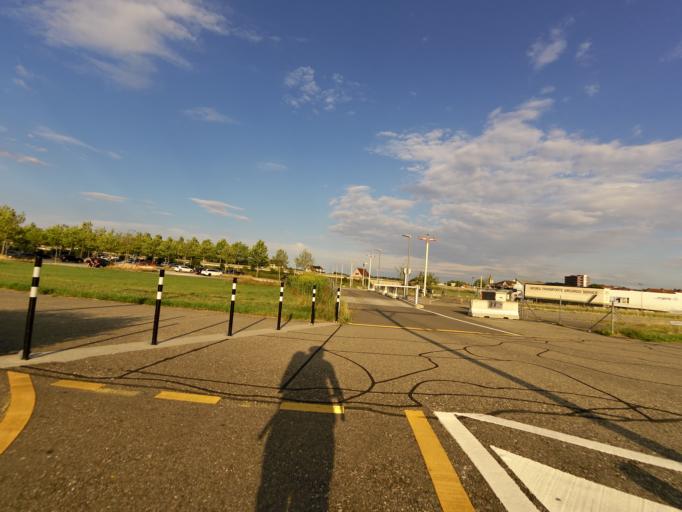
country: CH
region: Zurich
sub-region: Bezirk Buelach
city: Kloten / Horainli
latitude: 47.4563
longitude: 8.5764
